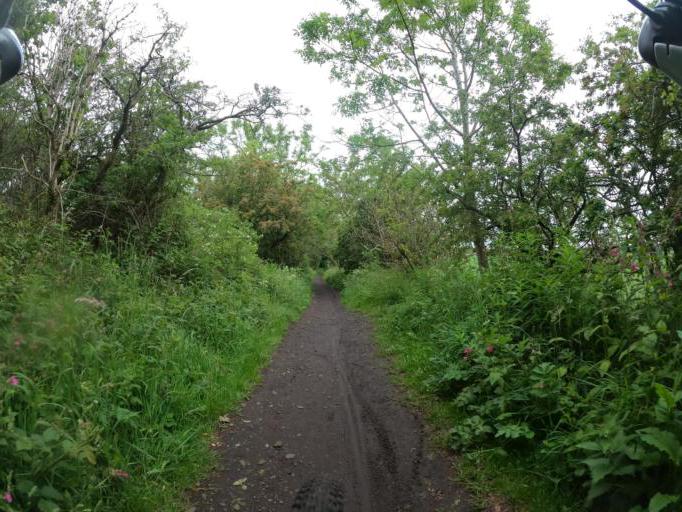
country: GB
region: Scotland
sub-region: Edinburgh
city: Currie
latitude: 55.9059
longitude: -3.3026
